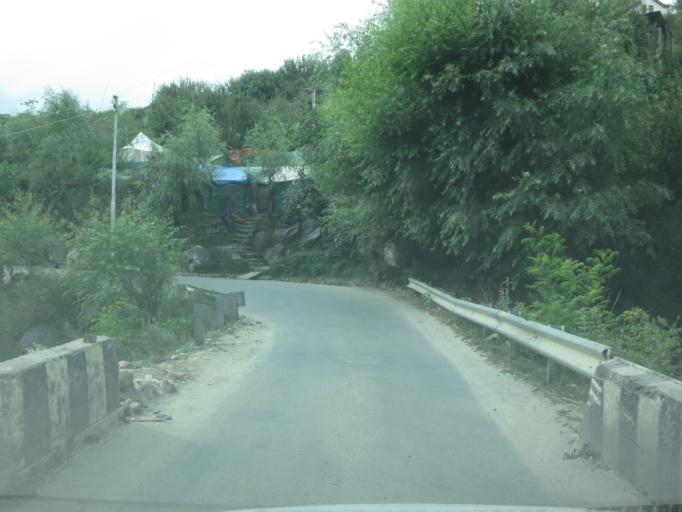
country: IN
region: Himachal Pradesh
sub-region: Kulu
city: Manali
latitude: 32.2196
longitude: 77.2002
